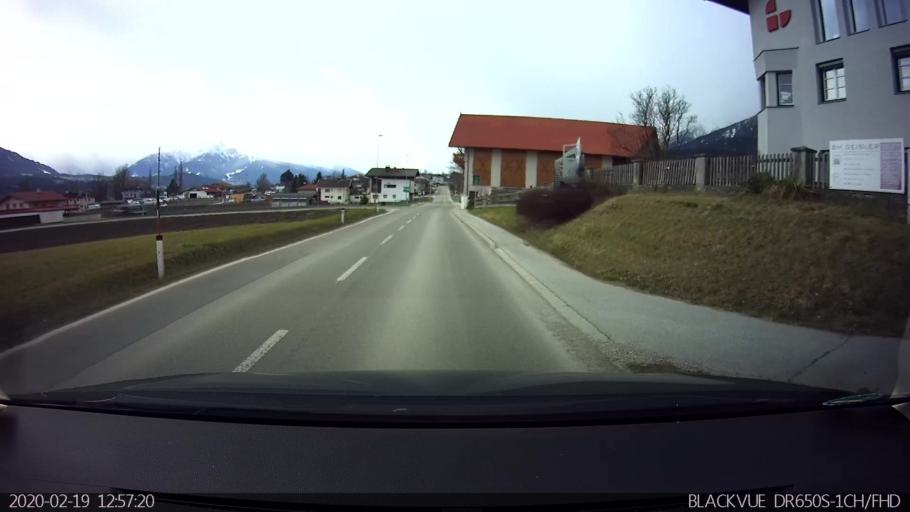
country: AT
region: Tyrol
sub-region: Politischer Bezirk Innsbruck Land
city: Absam
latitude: 47.2940
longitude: 11.4845
